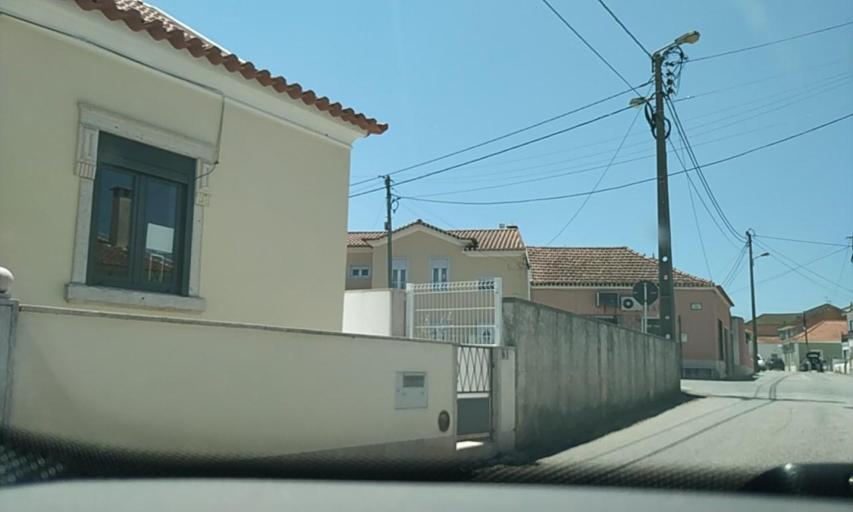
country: PT
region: Lisbon
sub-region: Sintra
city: Pero Pinheiro
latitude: 38.8467
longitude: -9.3390
